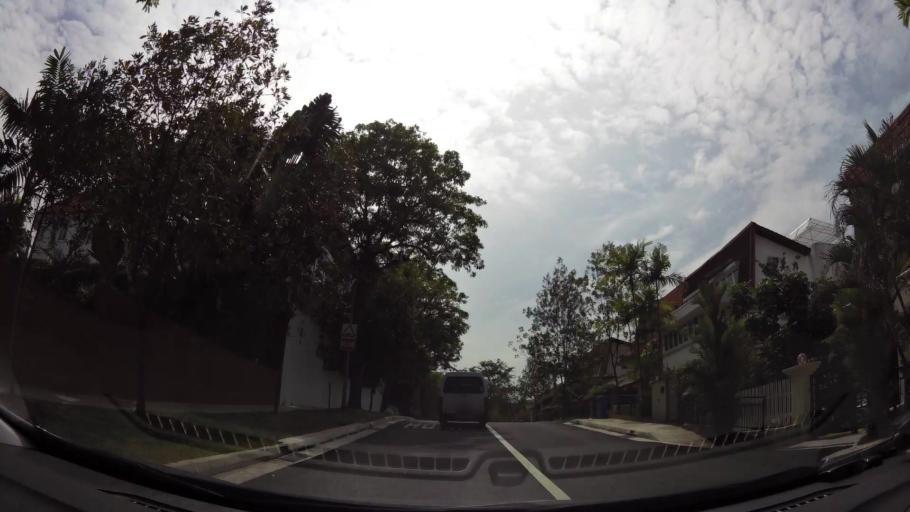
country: SG
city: Singapore
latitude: 1.3205
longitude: 103.7589
